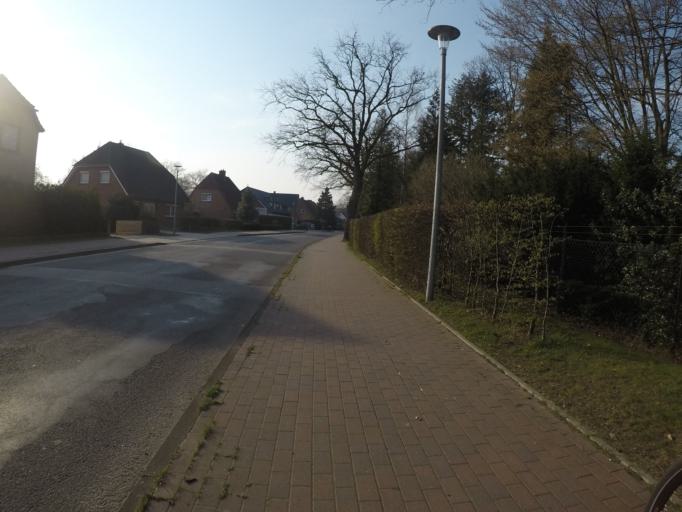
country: DE
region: Schleswig-Holstein
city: Rickling
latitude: 53.9981
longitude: 10.1721
